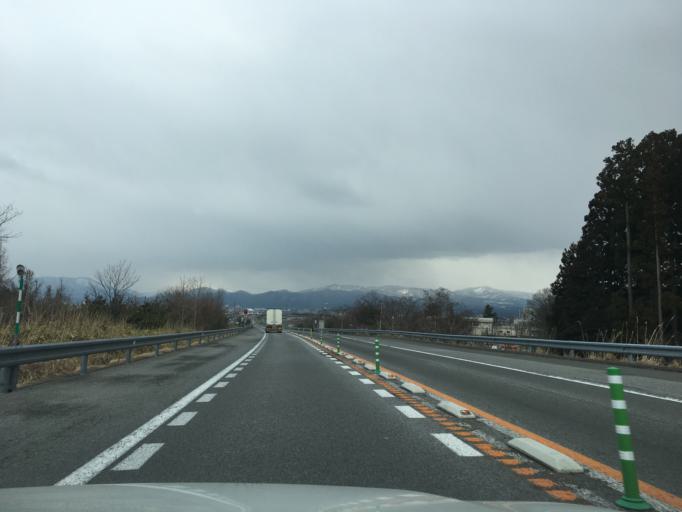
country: JP
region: Aomori
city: Aomori Shi
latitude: 40.7976
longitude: 140.7068
